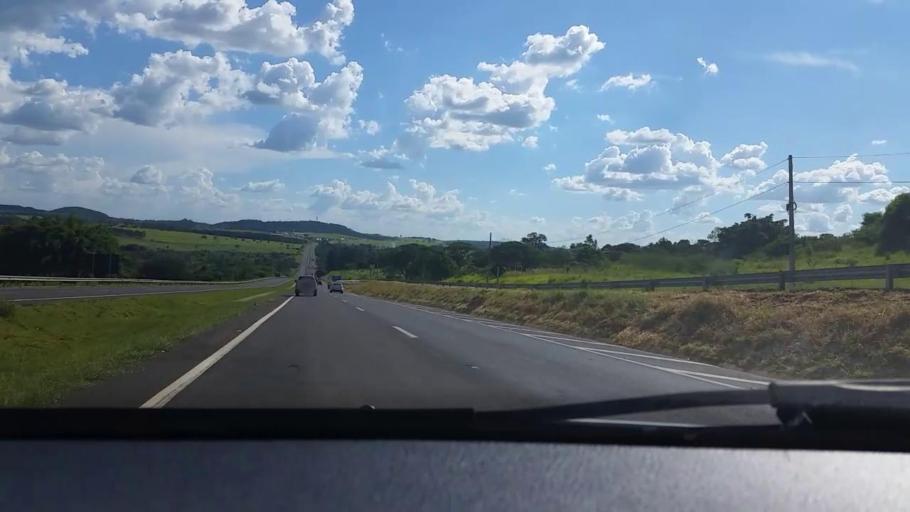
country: BR
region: Sao Paulo
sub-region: Bauru
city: Bauru
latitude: -22.3992
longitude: -49.0890
